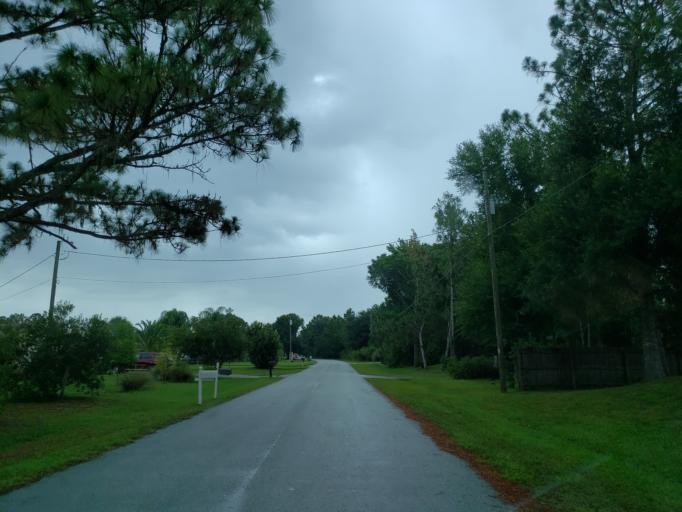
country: US
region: Florida
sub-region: Pasco County
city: Wesley Chapel
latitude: 28.2630
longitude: -82.3720
